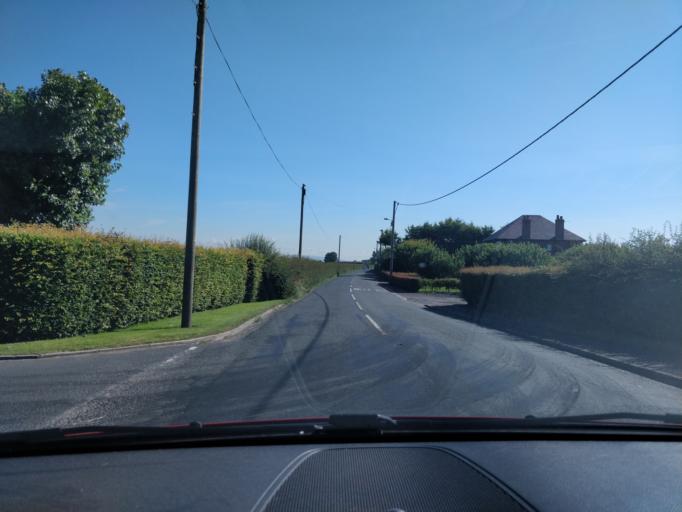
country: GB
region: England
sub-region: Lancashire
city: Banks
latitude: 53.6975
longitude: -2.8868
